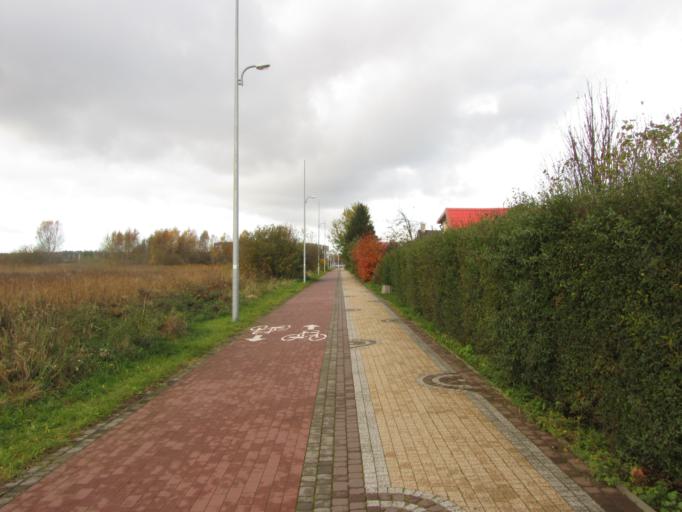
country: PL
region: West Pomeranian Voivodeship
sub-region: Powiat kolobrzeski
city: Grzybowo
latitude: 54.1679
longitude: 15.5325
